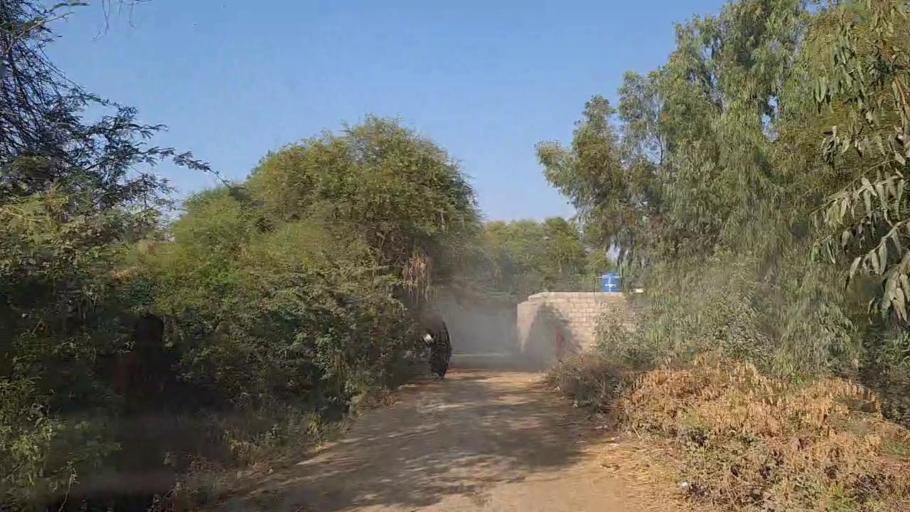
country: PK
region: Sindh
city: Thatta
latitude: 24.7680
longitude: 67.9670
